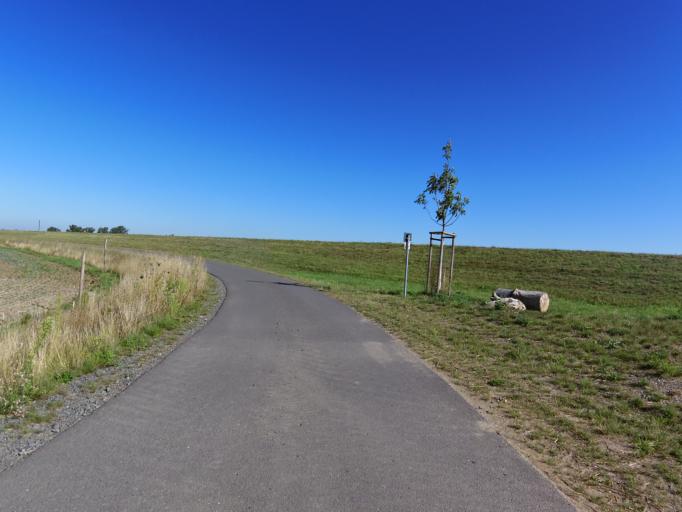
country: DE
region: Saxony
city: Torgau
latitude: 51.6113
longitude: 12.9955
